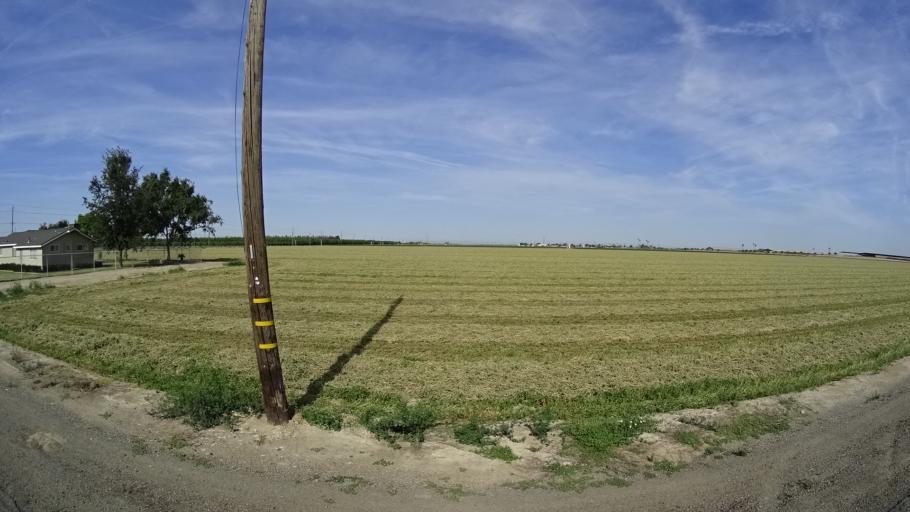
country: US
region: California
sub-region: Tulare County
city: Goshen
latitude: 36.3438
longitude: -119.4929
